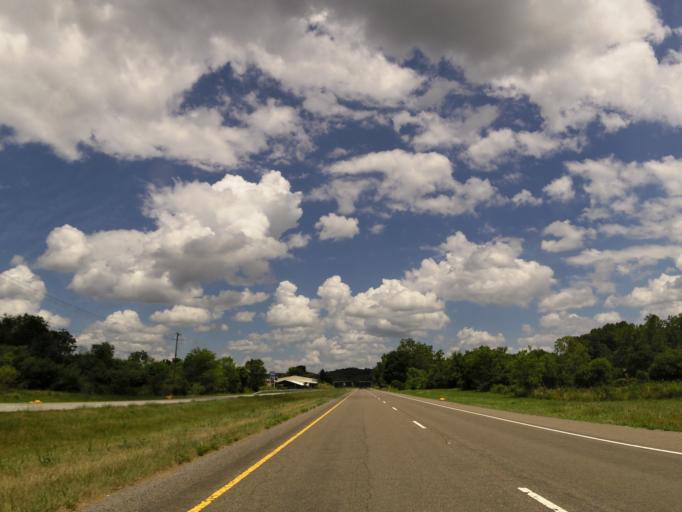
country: US
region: Tennessee
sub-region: Claiborne County
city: Tazewell
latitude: 36.6368
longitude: -83.4377
